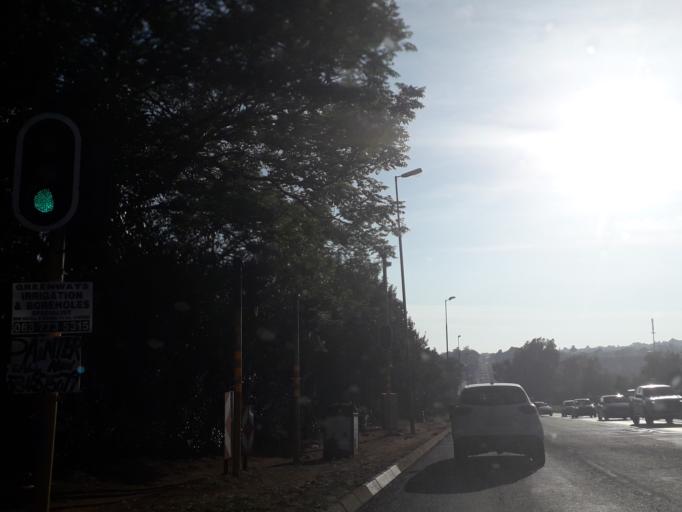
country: ZA
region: Gauteng
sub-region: City of Johannesburg Metropolitan Municipality
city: Roodepoort
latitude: -26.0994
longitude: 27.9087
